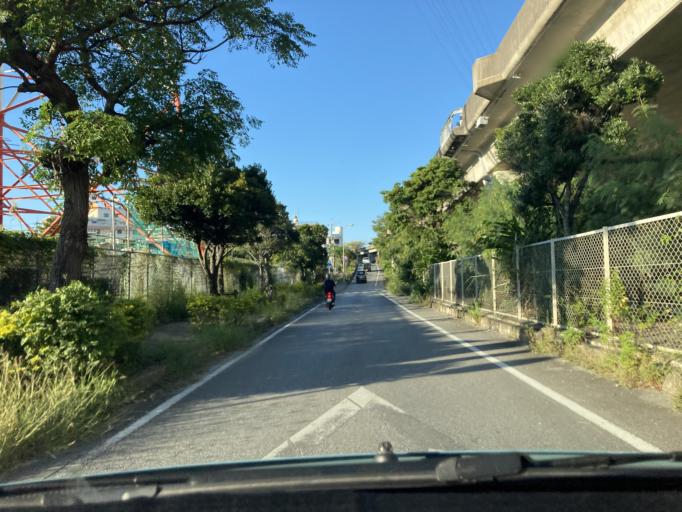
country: JP
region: Okinawa
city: Tomigusuku
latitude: 26.1965
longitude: 127.7396
